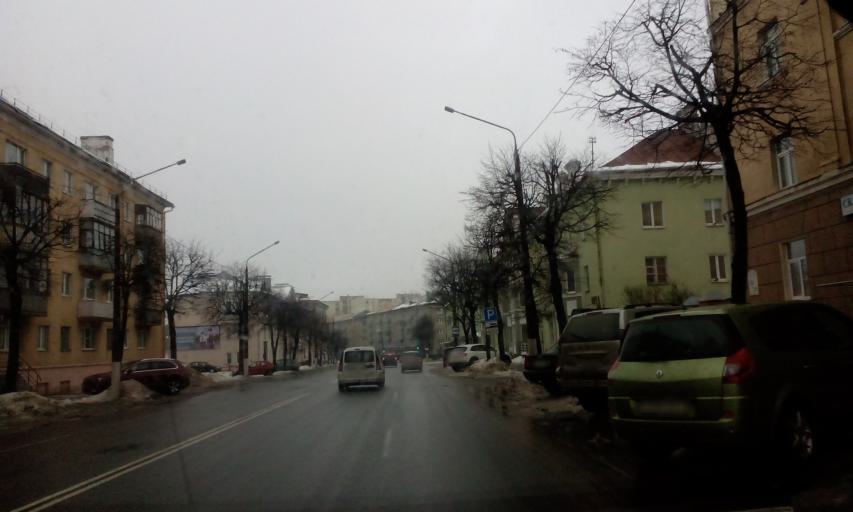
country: BY
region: Mogilev
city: Mahilyow
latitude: 53.9020
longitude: 30.3430
